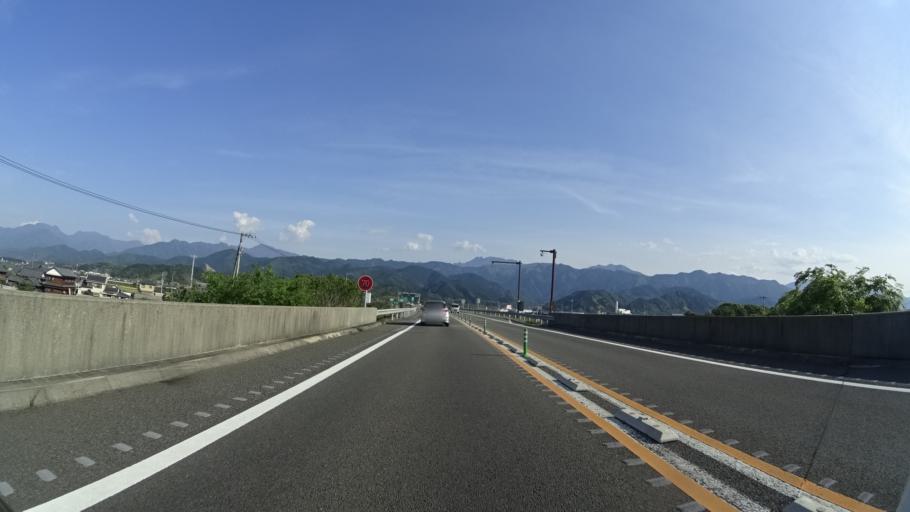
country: JP
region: Ehime
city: Saijo
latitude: 33.9011
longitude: 133.0762
